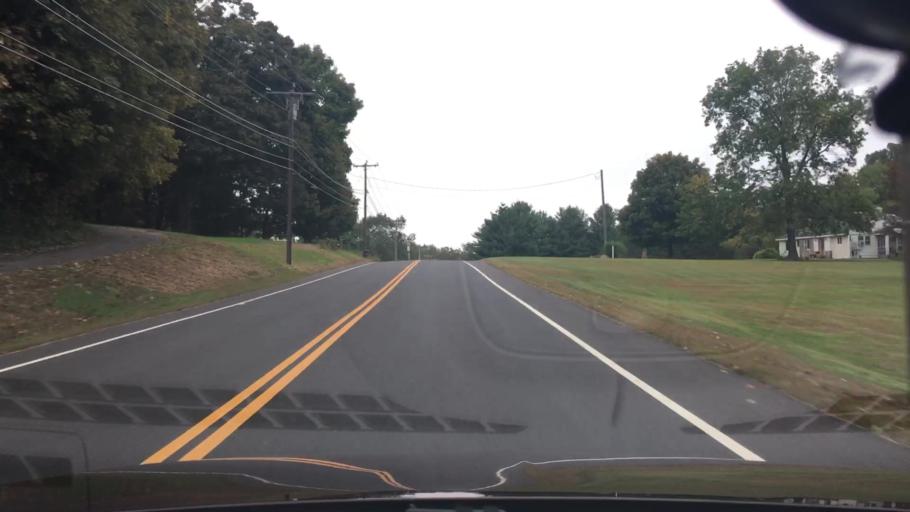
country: US
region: Connecticut
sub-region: Tolland County
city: Somers
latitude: 42.0012
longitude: -72.4537
